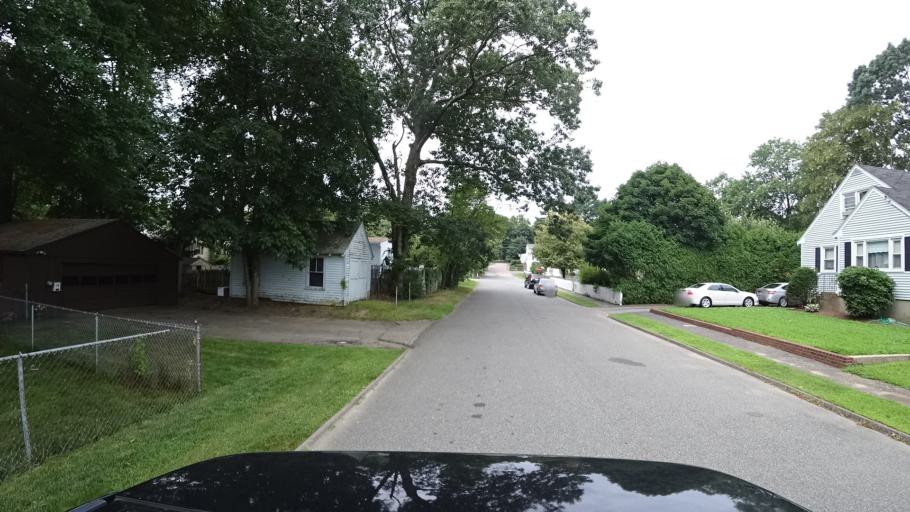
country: US
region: Massachusetts
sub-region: Norfolk County
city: Dedham
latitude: 42.2226
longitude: -71.1637
